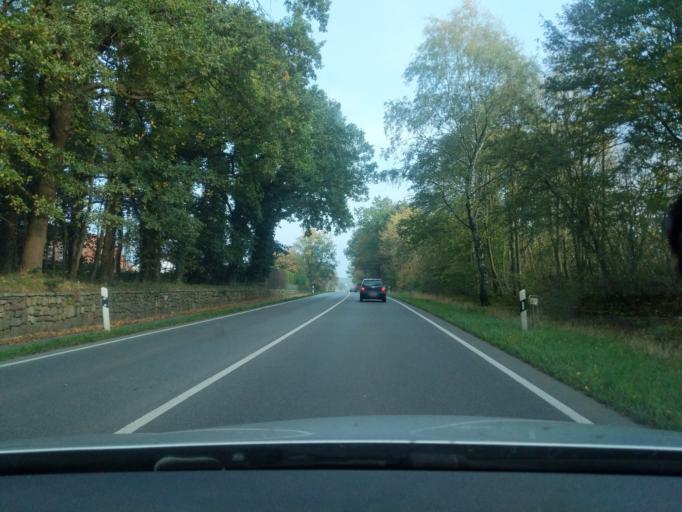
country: DE
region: Lower Saxony
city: Hammah
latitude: 53.5939
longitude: 9.4129
